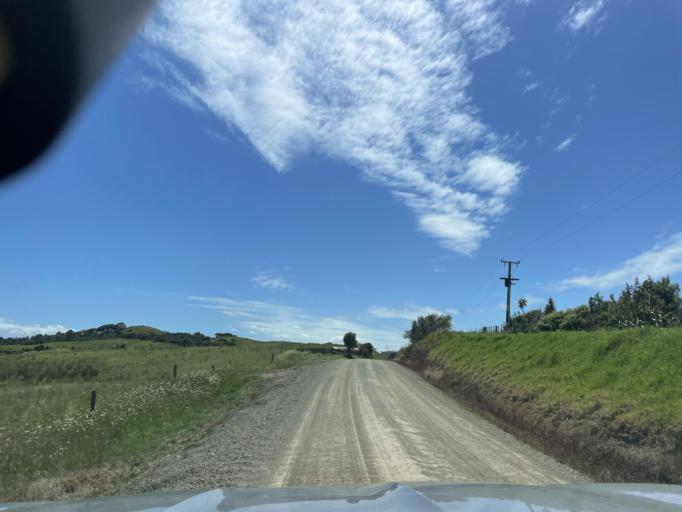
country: NZ
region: Auckland
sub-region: Auckland
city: Wellsford
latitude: -36.2230
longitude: 174.3631
